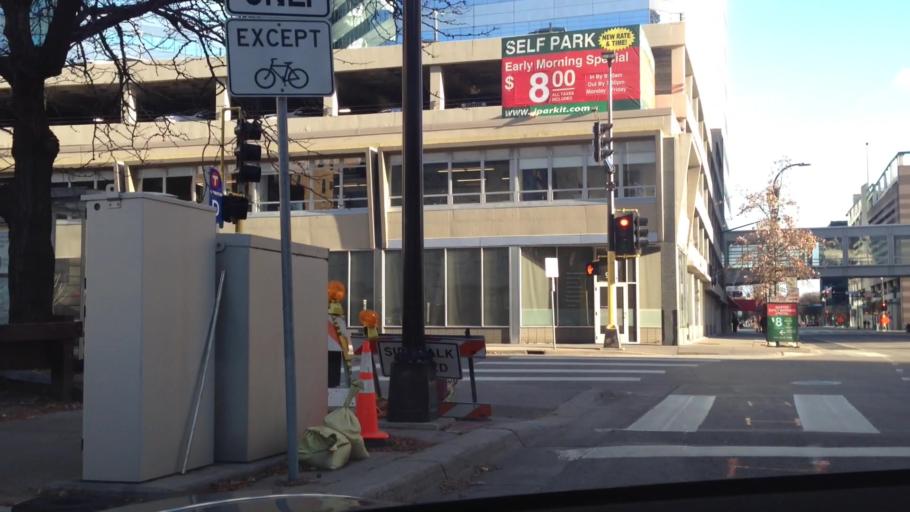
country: US
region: Minnesota
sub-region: Hennepin County
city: Minneapolis
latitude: 44.9736
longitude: -93.2736
